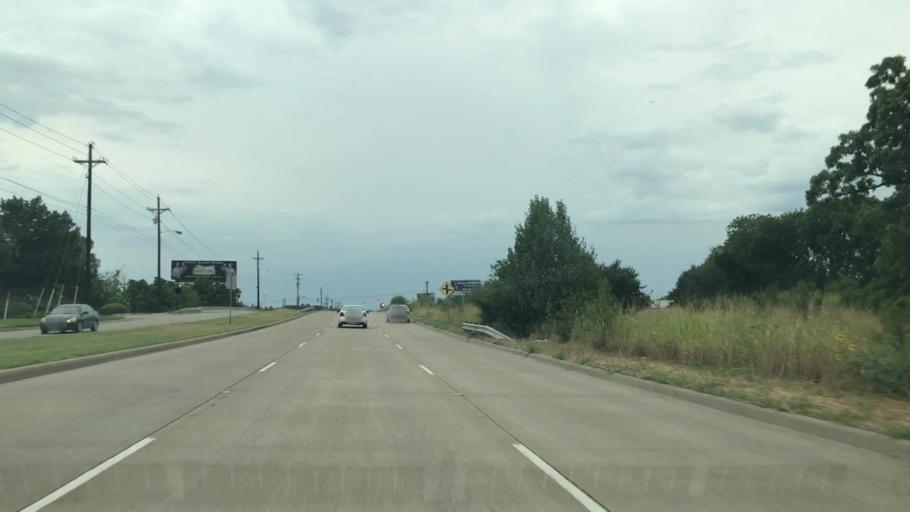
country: US
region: Texas
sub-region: Dallas County
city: Carrollton
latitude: 32.9513
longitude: -96.9373
